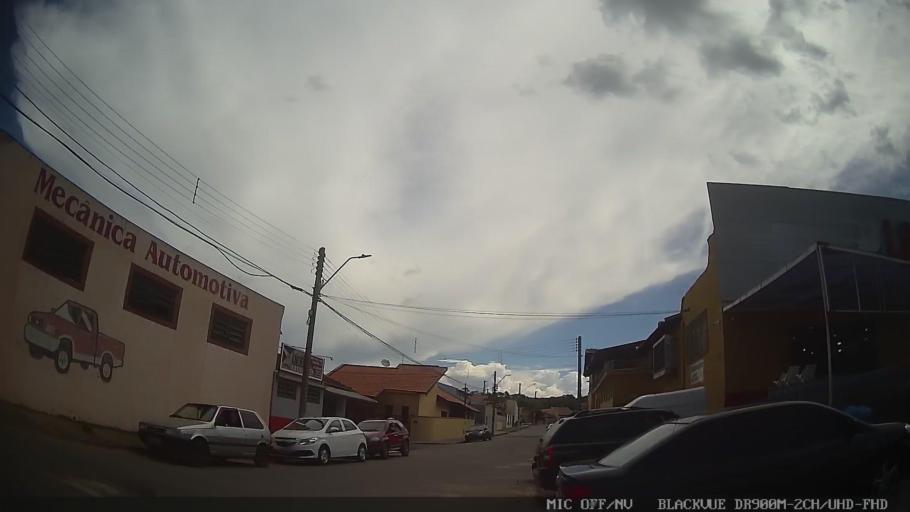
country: BR
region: Sao Paulo
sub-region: Conchas
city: Conchas
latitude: -23.0150
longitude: -48.0043
